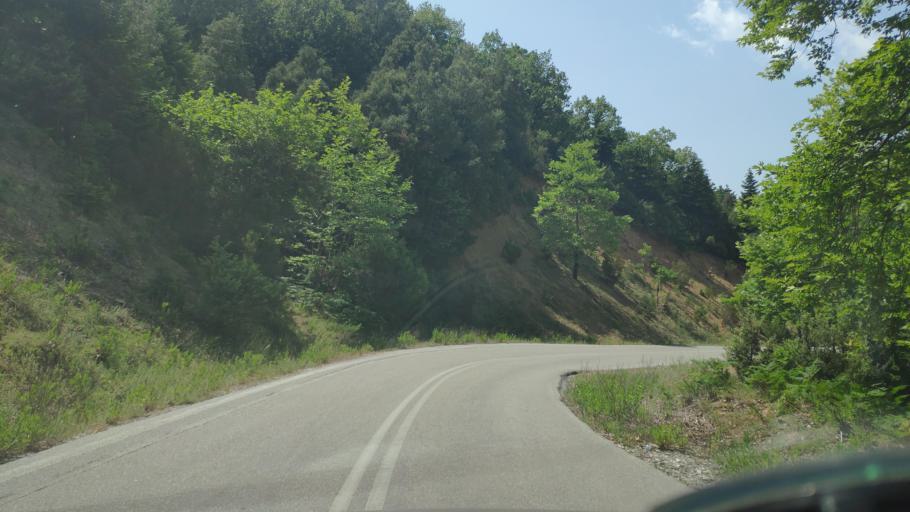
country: GR
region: Epirus
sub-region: Nomos Artas
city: Ano Kalentini
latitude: 39.2398
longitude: 21.2127
